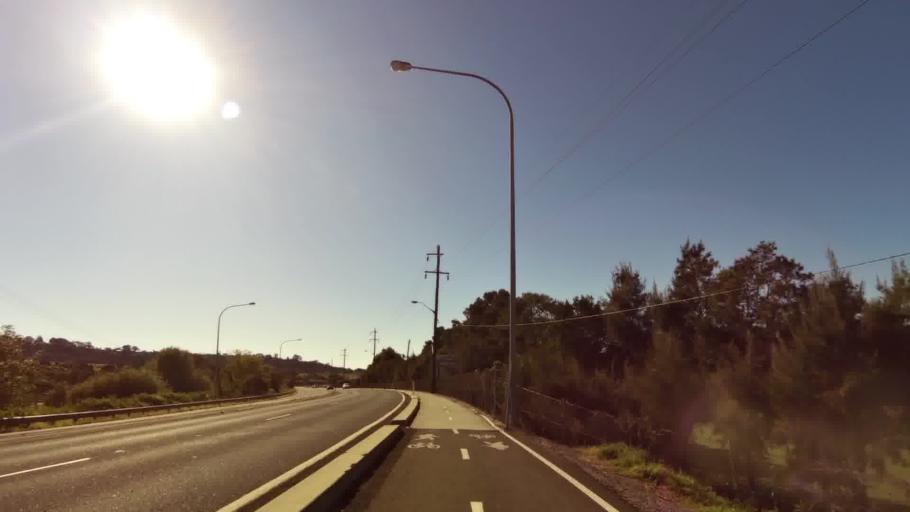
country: AU
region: New South Wales
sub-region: Wollongong
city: Koonawarra
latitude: -34.4741
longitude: 150.8133
